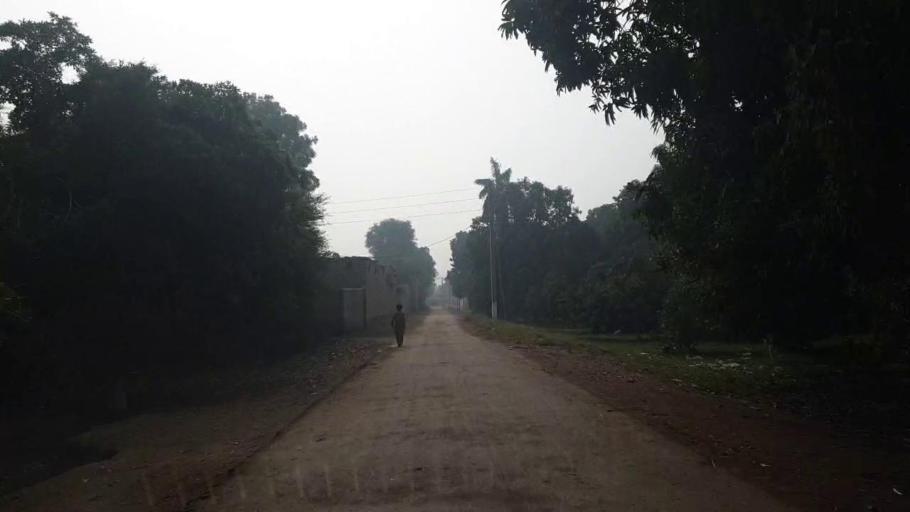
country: PK
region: Sindh
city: Tando Adam
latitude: 25.7847
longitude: 68.5962
